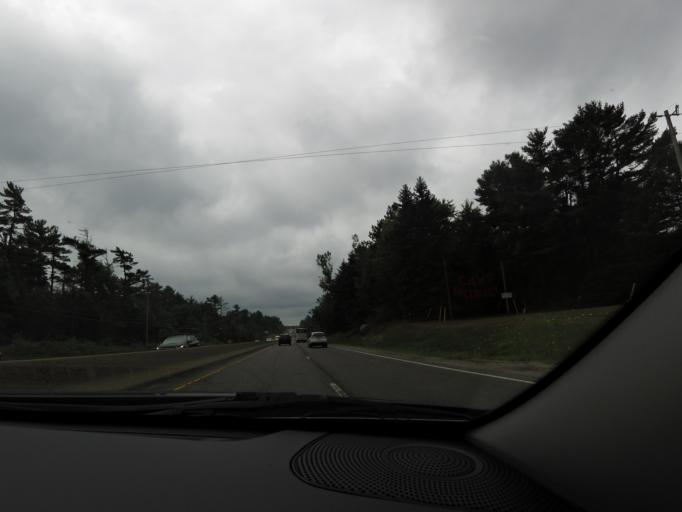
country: CA
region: Ontario
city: Gravenhurst
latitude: 44.8335
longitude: -79.3204
